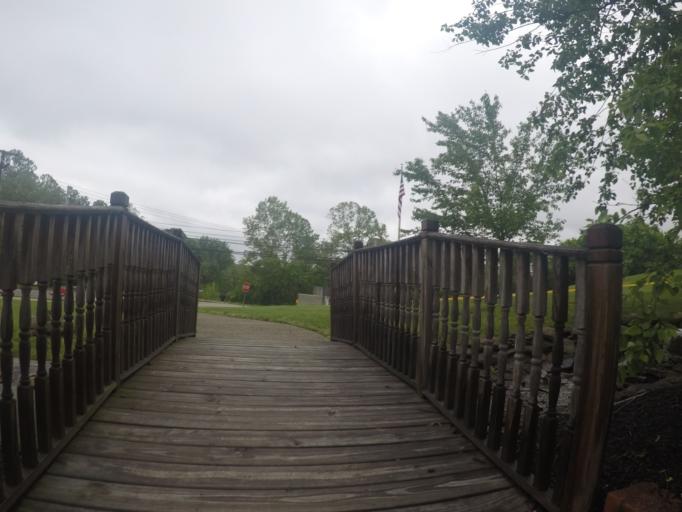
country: US
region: West Virginia
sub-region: Cabell County
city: Barboursville
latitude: 38.4103
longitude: -82.2951
